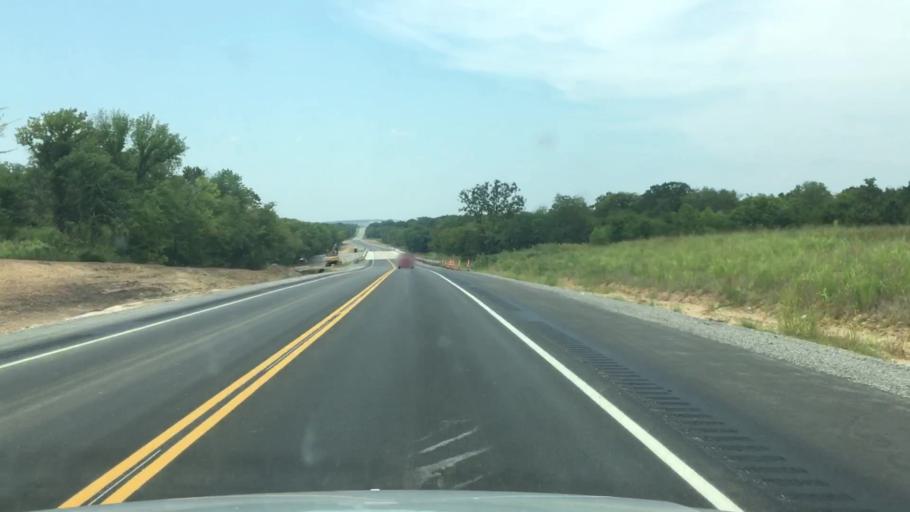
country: US
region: Oklahoma
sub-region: Muskogee County
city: Fort Gibson
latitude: 35.9370
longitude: -95.1734
